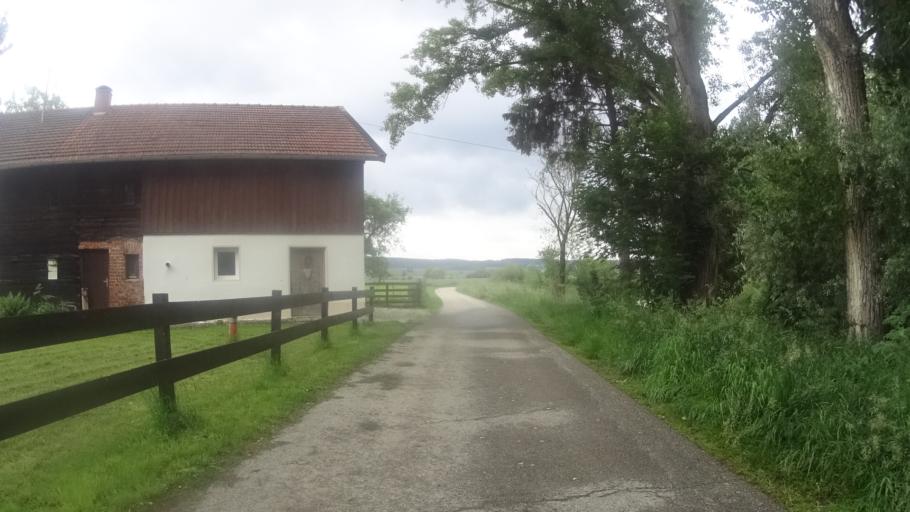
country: DE
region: Bavaria
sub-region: Lower Bavaria
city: Triftern
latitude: 48.4408
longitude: 13.0158
